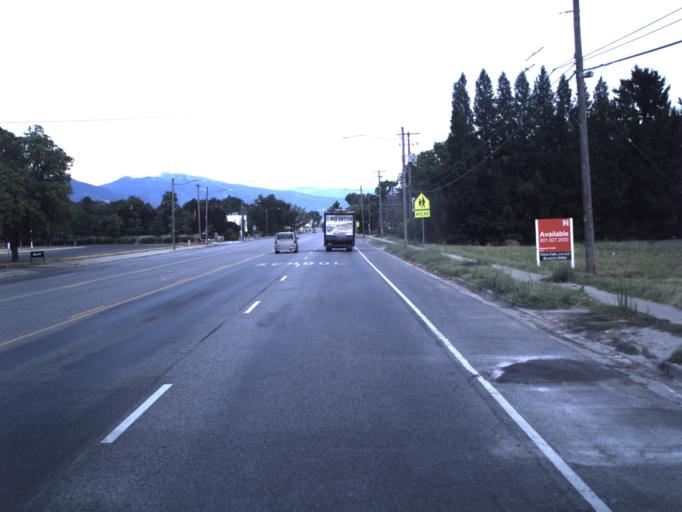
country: US
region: Utah
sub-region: Davis County
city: Clearfield
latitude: 41.1012
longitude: -112.0132
